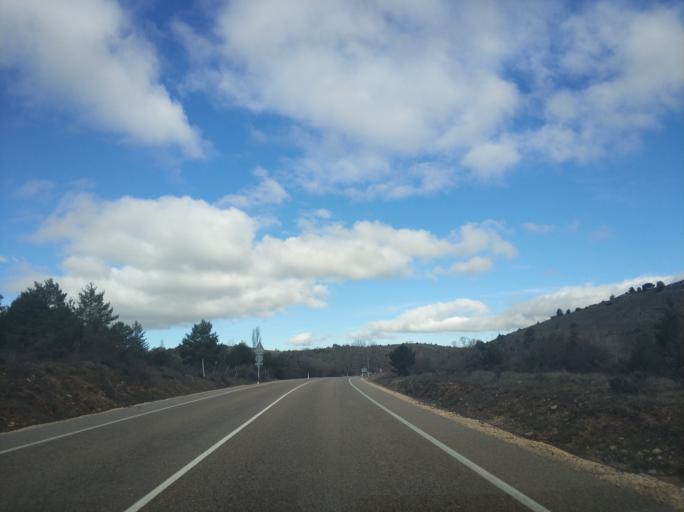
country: ES
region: Castille and Leon
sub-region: Provincia de Burgos
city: Rabanera del Pinar
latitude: 41.8787
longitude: -3.2239
